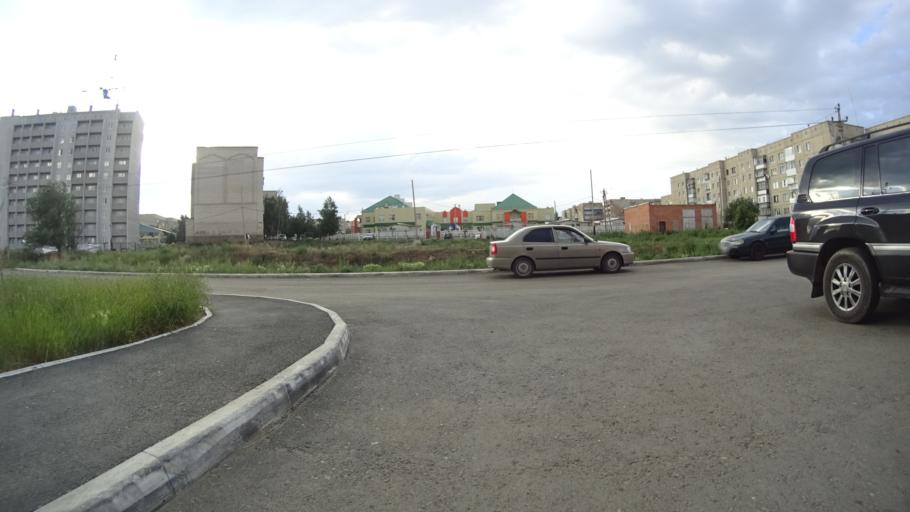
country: RU
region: Chelyabinsk
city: Troitsk
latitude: 54.0717
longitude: 61.5317
